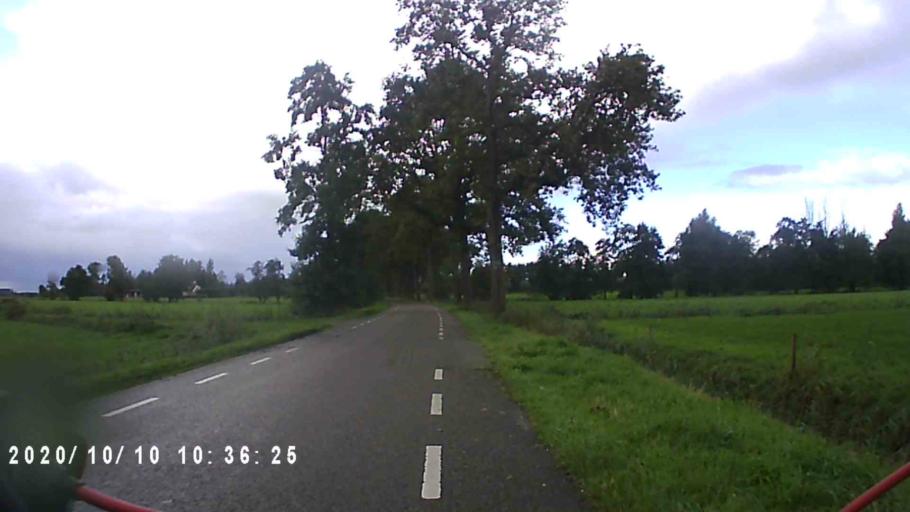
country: NL
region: Groningen
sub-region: Gemeente Grootegast
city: Grootegast
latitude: 53.1870
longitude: 6.3041
